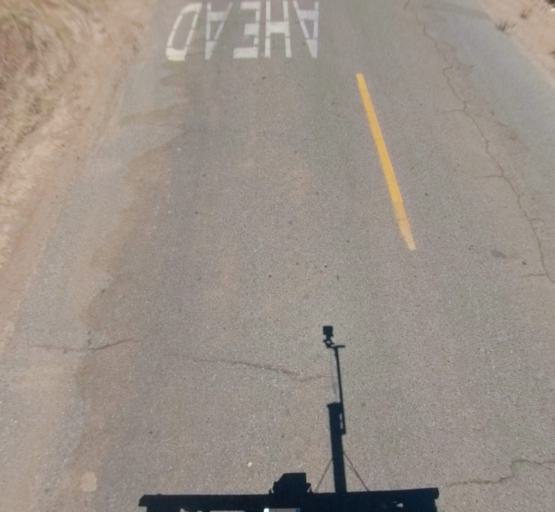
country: US
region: California
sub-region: Madera County
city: Madera Acres
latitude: 37.0981
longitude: -120.0761
